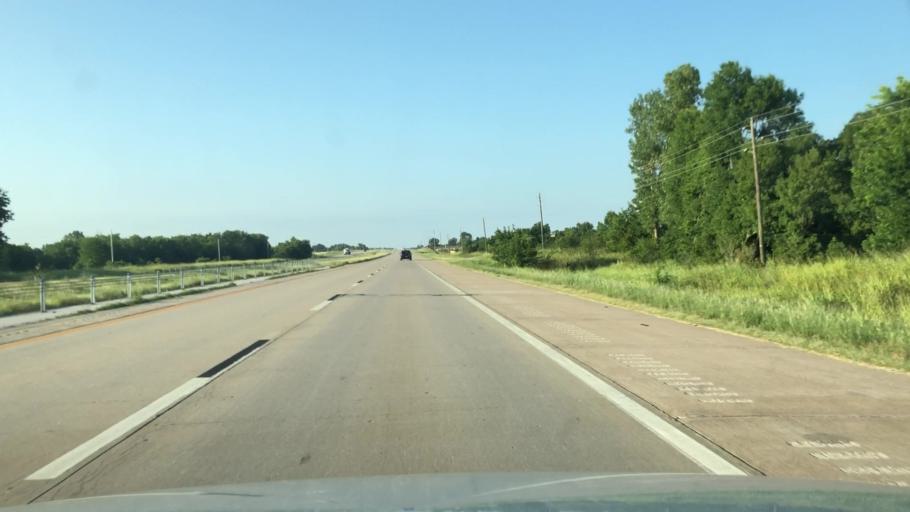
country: US
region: Oklahoma
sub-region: Osage County
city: Skiatook
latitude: 36.4716
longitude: -95.9207
